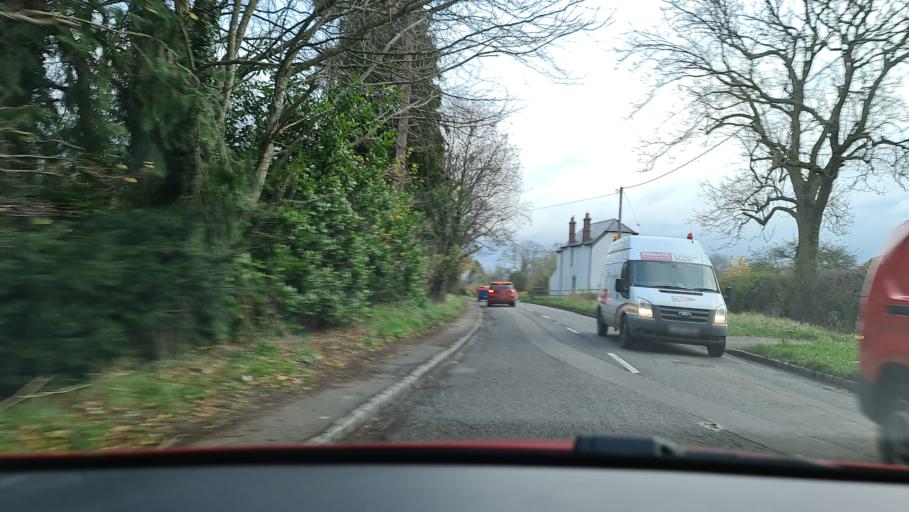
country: GB
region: England
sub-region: Buckinghamshire
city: Weston Turville
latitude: 51.7663
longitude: -0.7837
